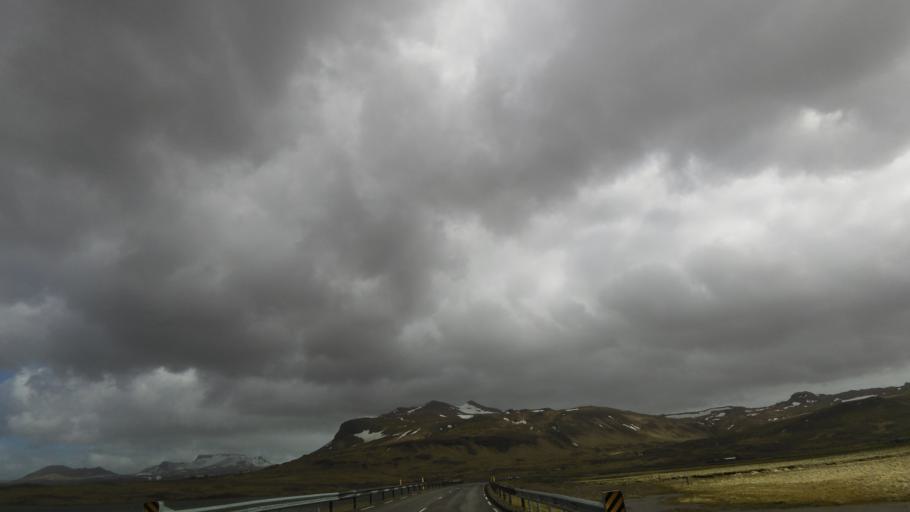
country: IS
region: West
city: Olafsvik
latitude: 64.8918
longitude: -23.6176
